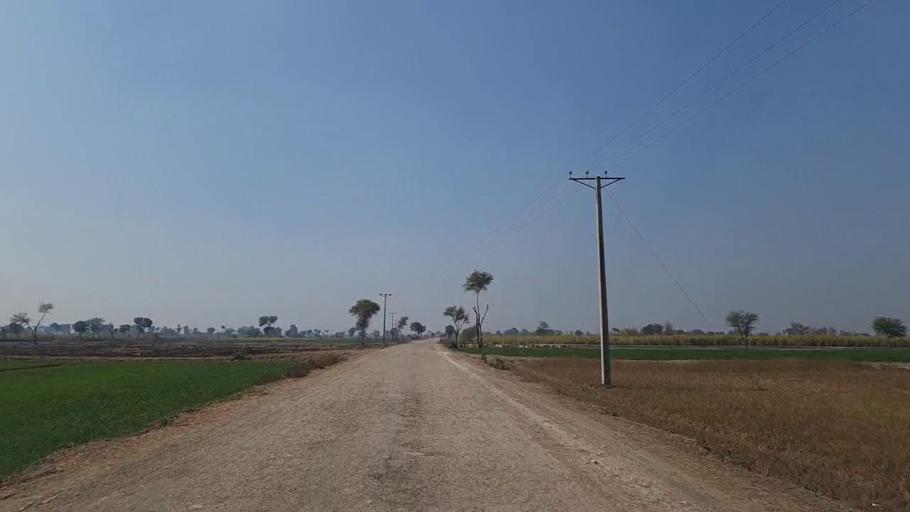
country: PK
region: Sindh
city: Daur
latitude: 26.5032
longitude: 68.3188
